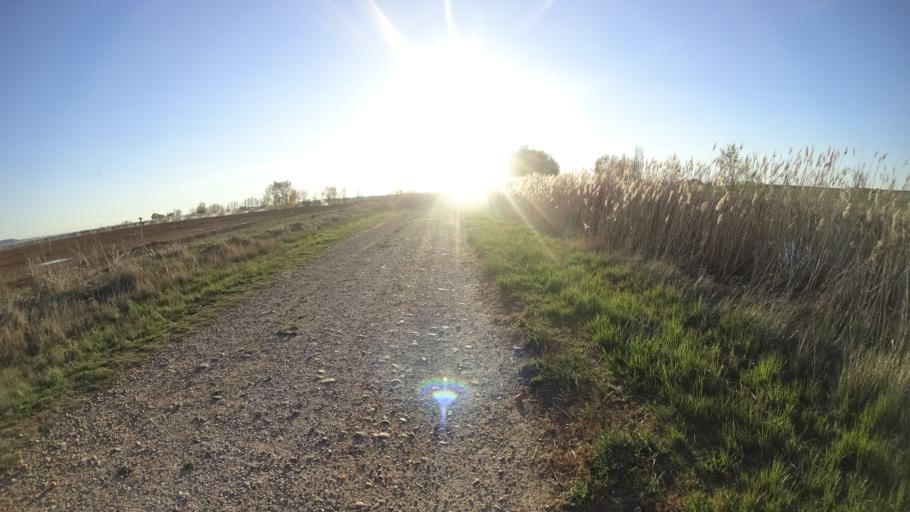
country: ES
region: Castille and Leon
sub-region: Provincia de Palencia
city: Fromista
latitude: 42.2583
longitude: -4.3799
